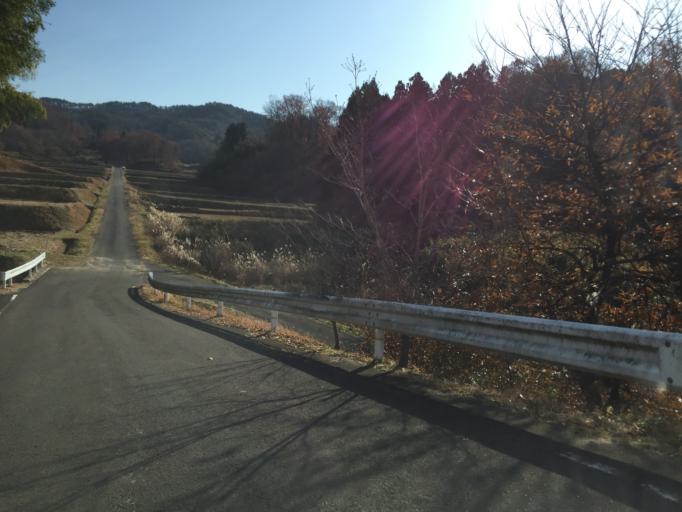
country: JP
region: Fukushima
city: Fukushima-shi
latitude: 37.7020
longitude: 140.5244
